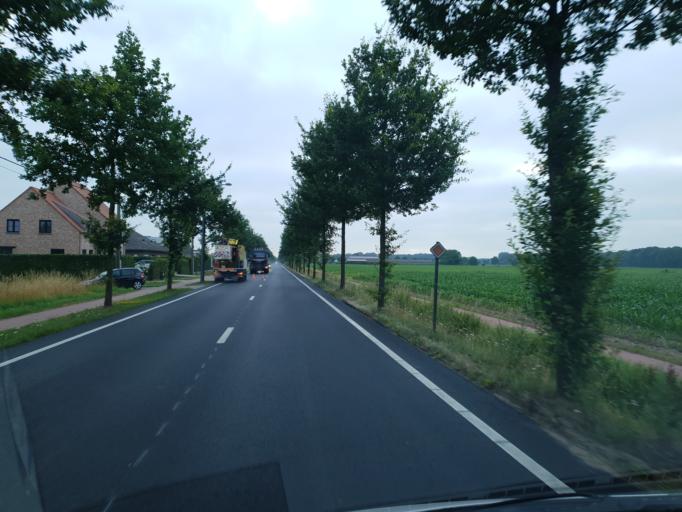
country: BE
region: Flanders
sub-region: Provincie Antwerpen
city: Rijkevorsel
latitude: 51.3739
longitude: 4.7163
